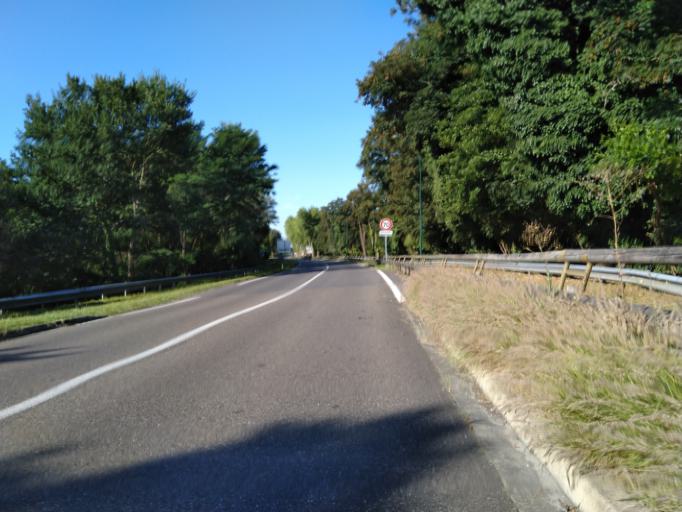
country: FR
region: Aquitaine
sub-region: Departement des Landes
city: Saint-Paul-les-Dax
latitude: 43.7329
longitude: -1.0335
